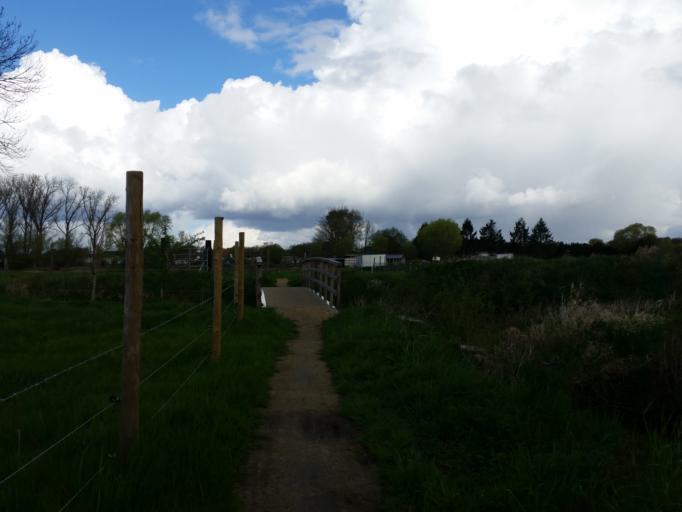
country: BE
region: Flanders
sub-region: Provincie Antwerpen
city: Mechelen
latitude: 50.9967
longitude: 4.5015
